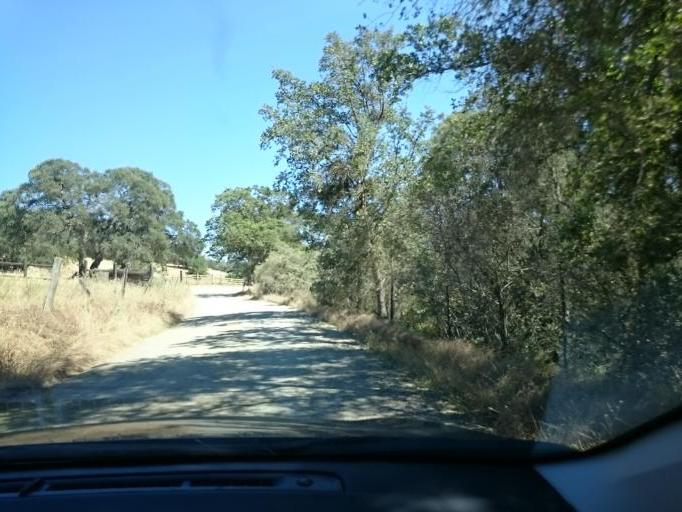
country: US
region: California
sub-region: Calaveras County
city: Rancho Calaveras
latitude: 38.1112
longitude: -120.7727
